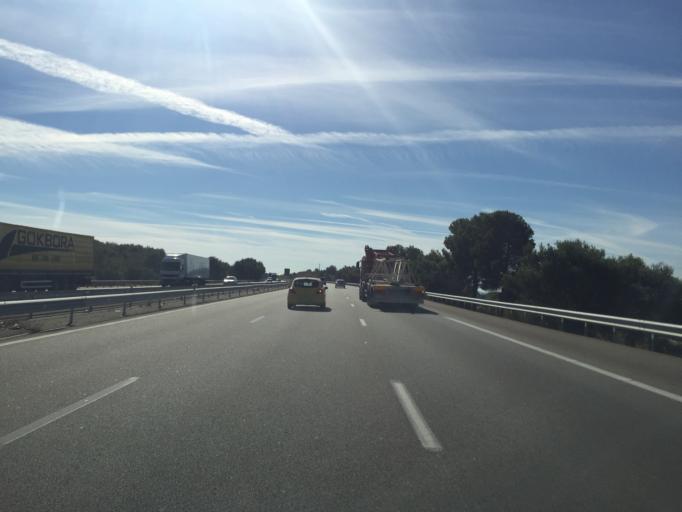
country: FR
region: Provence-Alpes-Cote d'Azur
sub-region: Departement des Bouches-du-Rhone
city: Salon-de-Provence
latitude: 43.6698
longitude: 5.0964
